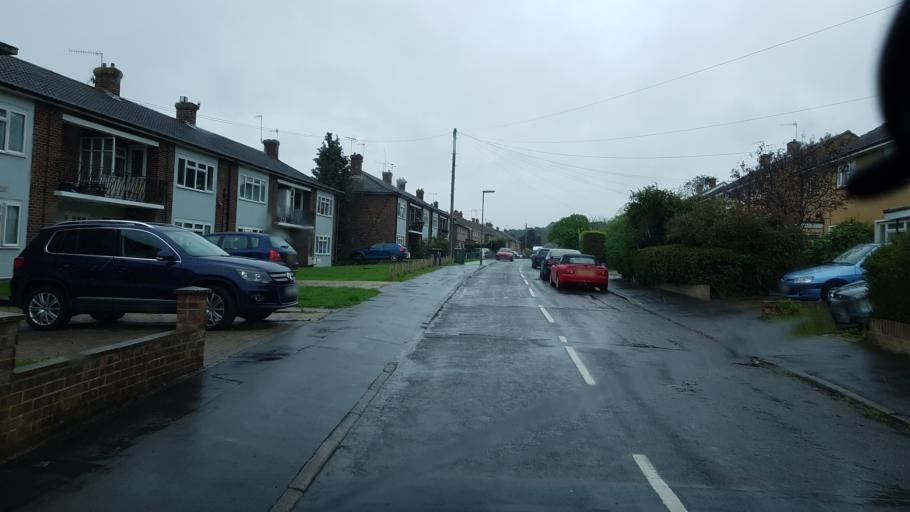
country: GB
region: England
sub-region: Surrey
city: Guildford
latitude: 51.2486
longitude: -0.6138
